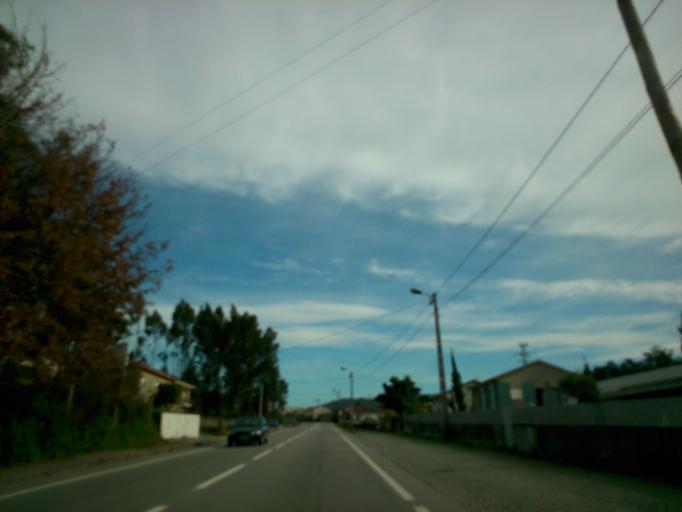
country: PT
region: Braga
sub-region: Barcelos
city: Barcelos
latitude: 41.5196
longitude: -8.5839
